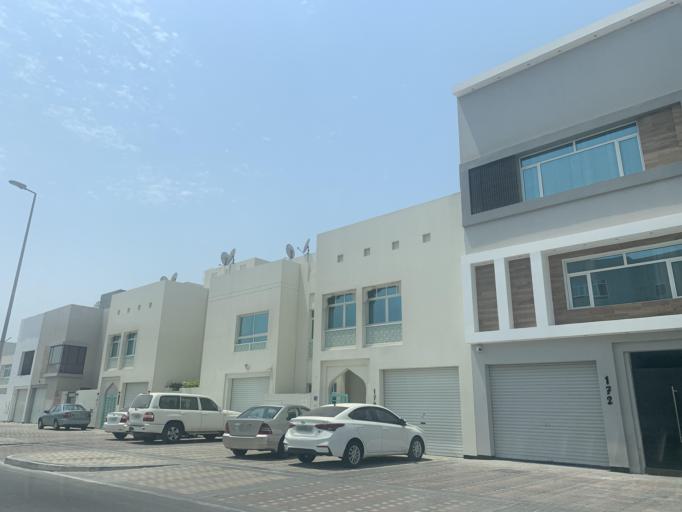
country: BH
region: Muharraq
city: Al Hadd
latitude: 26.2325
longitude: 50.6618
